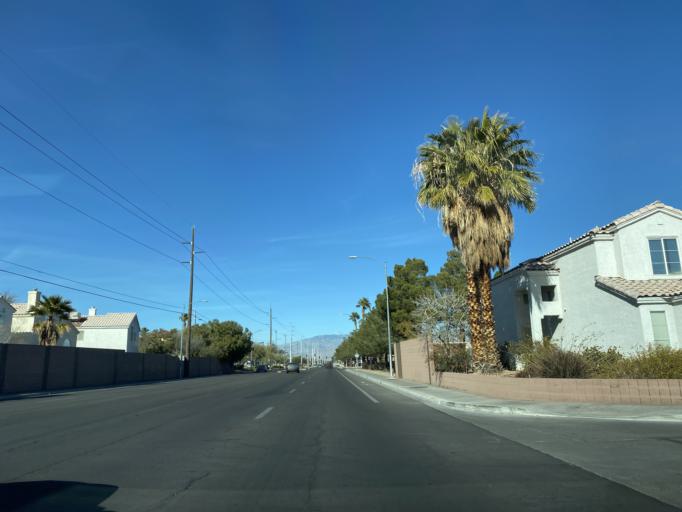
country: US
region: Nevada
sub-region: Clark County
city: Spring Valley
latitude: 36.1933
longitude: -115.2512
